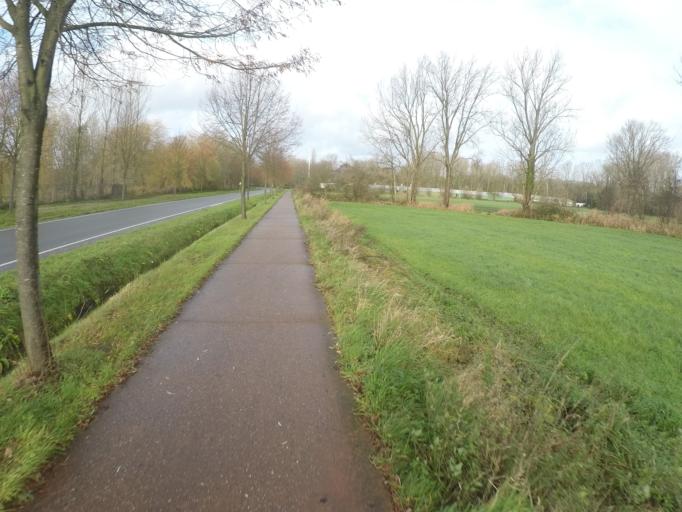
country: BE
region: Flanders
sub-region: Provincie Antwerpen
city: Wijnegem
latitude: 51.2188
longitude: 4.5264
